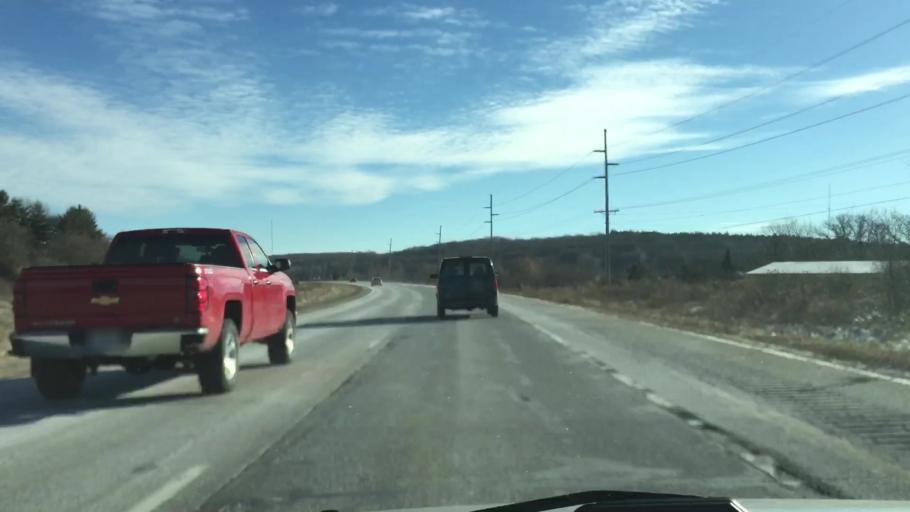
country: US
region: Wisconsin
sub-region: Walworth County
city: Como
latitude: 42.6158
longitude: -88.4537
